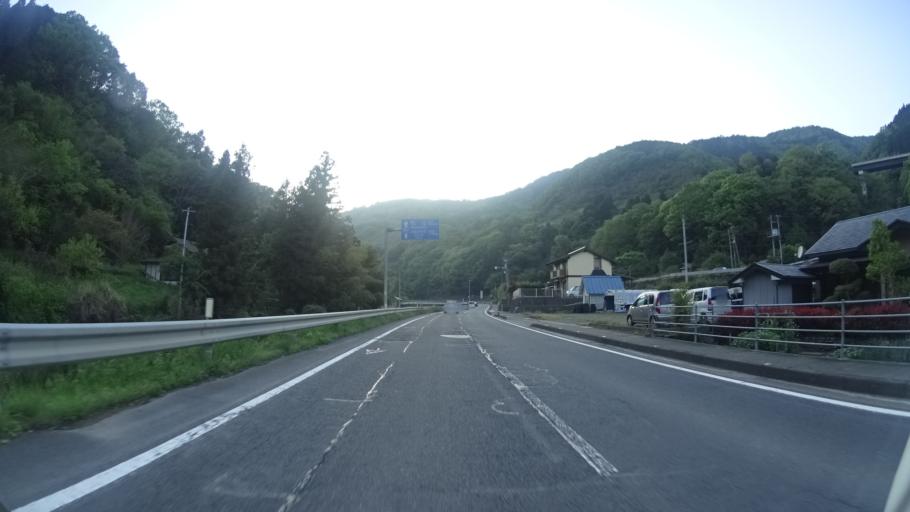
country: JP
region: Tokushima
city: Ikedacho
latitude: 34.0093
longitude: 133.7326
